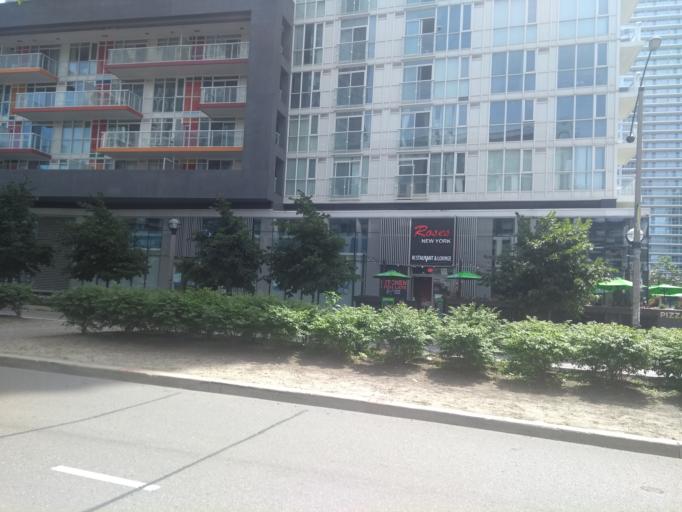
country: CA
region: Ontario
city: Toronto
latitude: 43.6395
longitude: -79.3993
